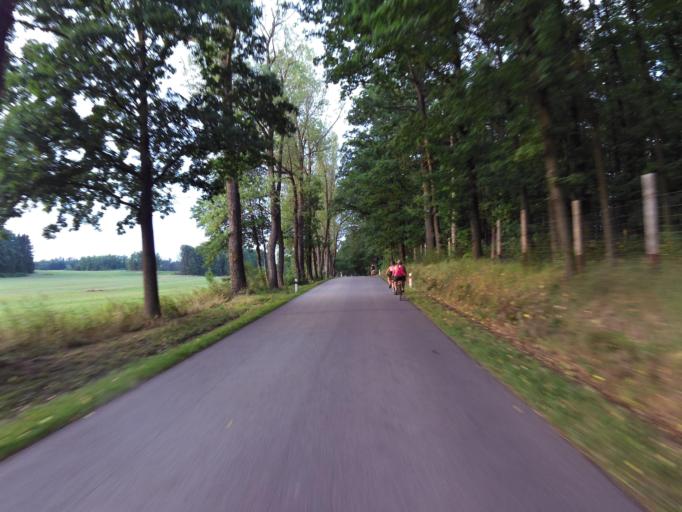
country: CZ
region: Jihocesky
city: Chlum u Trebone
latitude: 48.9673
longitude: 14.9388
